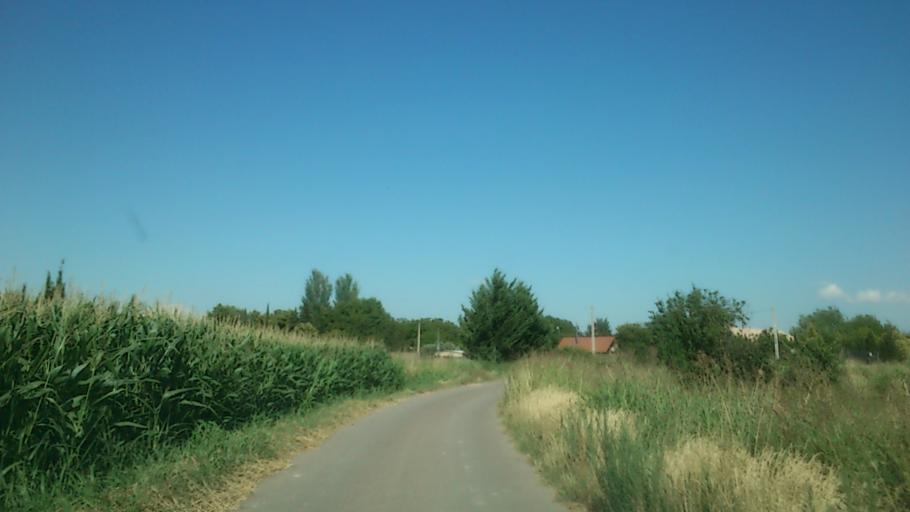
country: ES
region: Aragon
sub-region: Provincia de Zaragoza
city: Villanueva de Gallego
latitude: 41.6956
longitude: -0.8098
